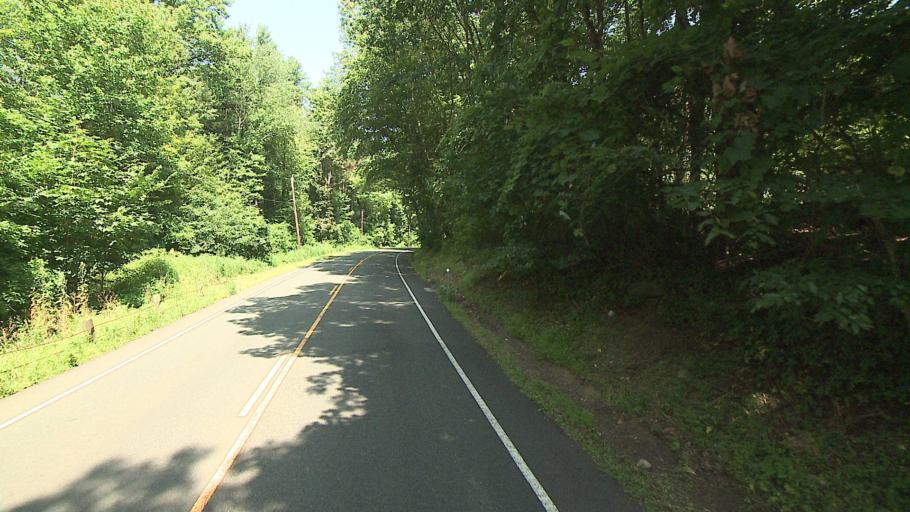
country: US
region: Connecticut
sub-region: Fairfield County
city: Trumbull
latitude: 41.2824
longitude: -73.2950
